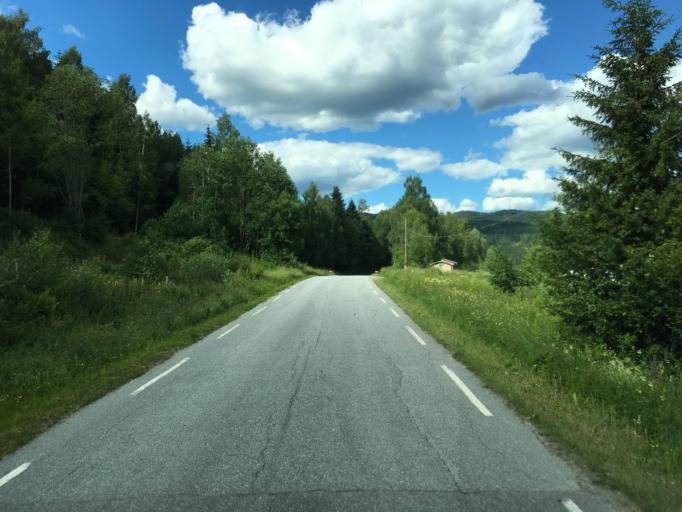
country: NO
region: Oppland
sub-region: Sondre Land
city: Hov
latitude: 60.5885
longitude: 10.2966
